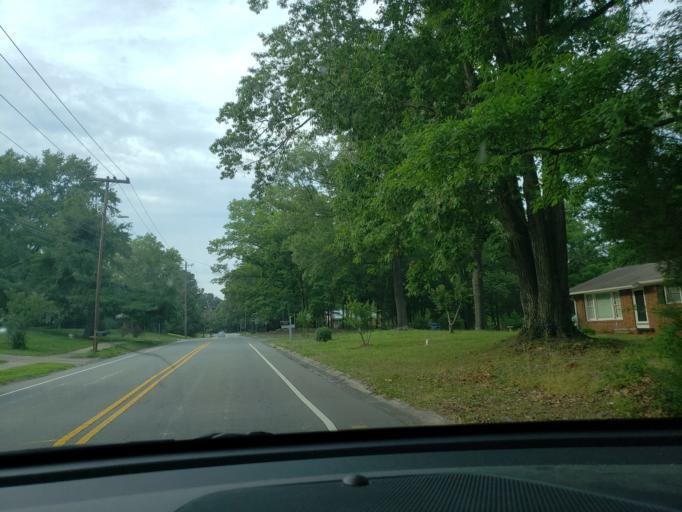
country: US
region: North Carolina
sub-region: Durham County
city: Durham
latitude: 35.8970
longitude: -78.9107
